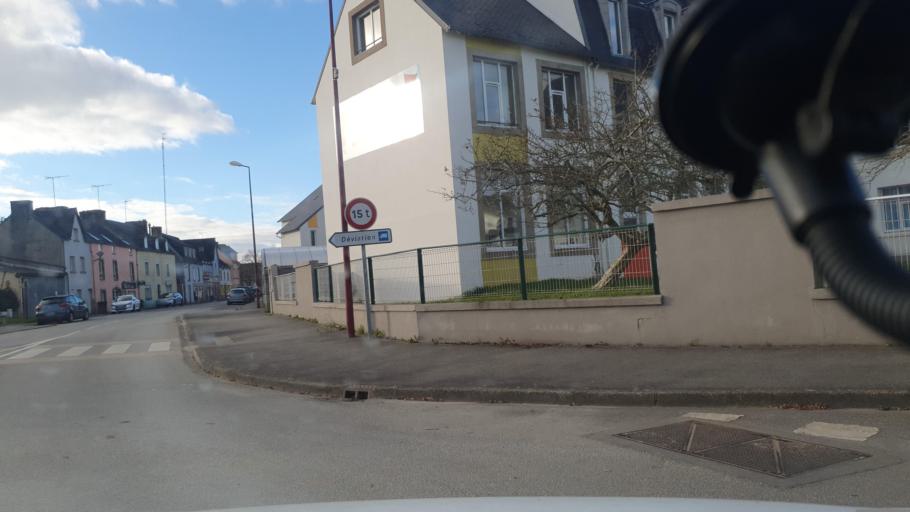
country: FR
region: Brittany
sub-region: Departement du Finistere
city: Briec
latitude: 48.1020
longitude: -3.9968
